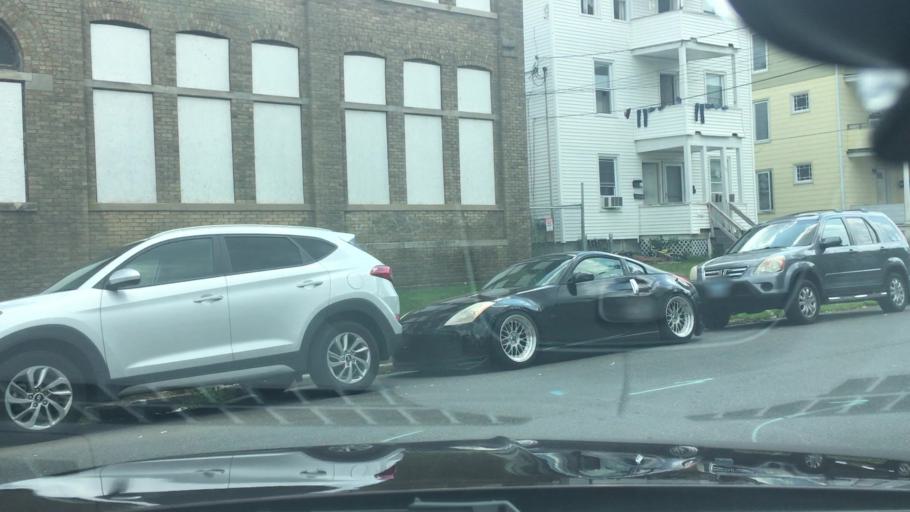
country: US
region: Connecticut
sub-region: Hartford County
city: New Britain
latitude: 41.6697
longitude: -72.7668
